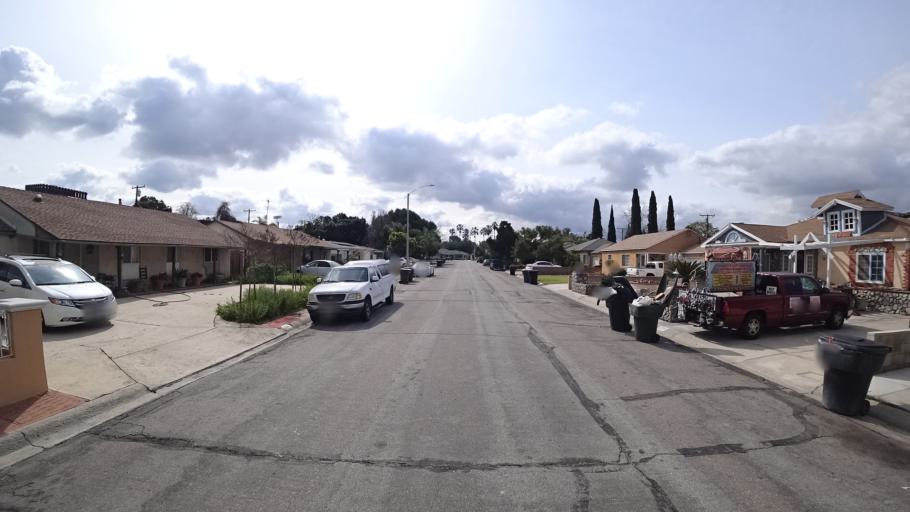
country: US
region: California
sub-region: Orange County
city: Buena Park
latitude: 33.8449
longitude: -117.9633
